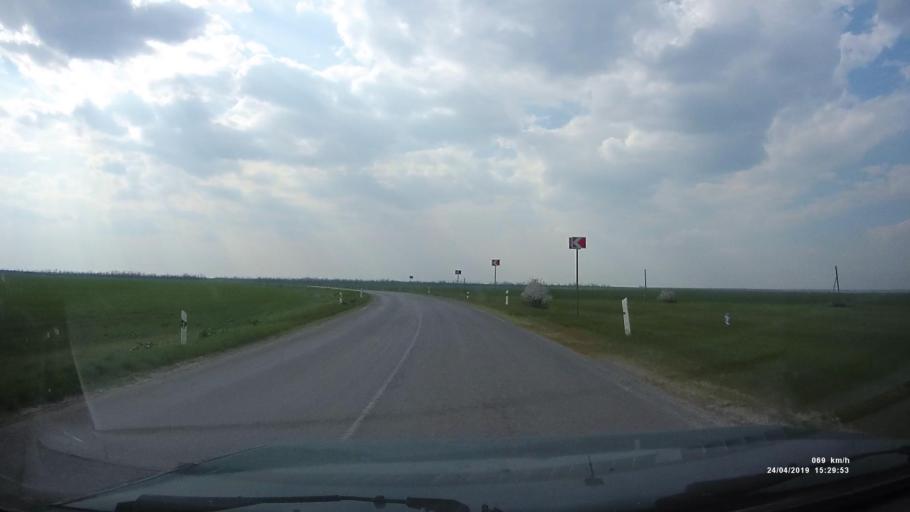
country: RU
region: Rostov
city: Remontnoye
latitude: 46.5992
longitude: 43.0175
